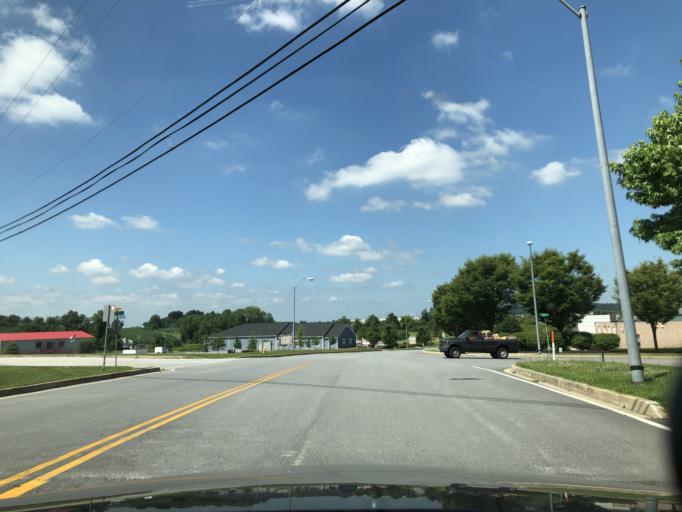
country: US
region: Maryland
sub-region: Carroll County
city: Westminster
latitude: 39.6071
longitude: -76.9905
